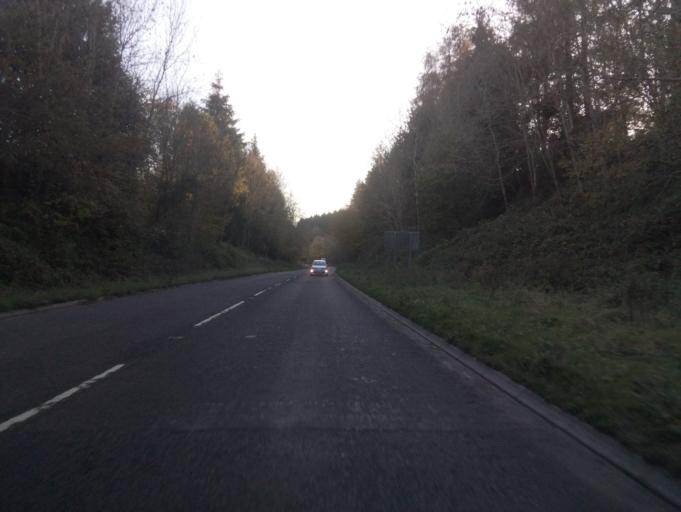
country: GB
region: England
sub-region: Wiltshire
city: Warminster
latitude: 51.1828
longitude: -2.1933
